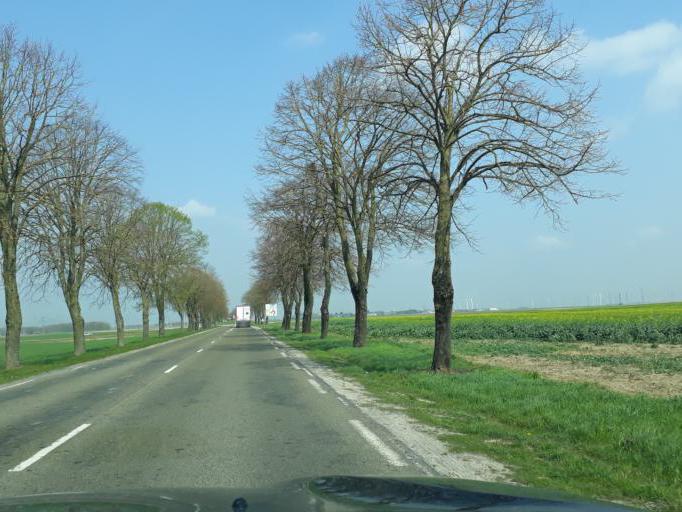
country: FR
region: Centre
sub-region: Departement du Loiret
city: Artenay
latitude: 48.0928
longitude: 1.8653
